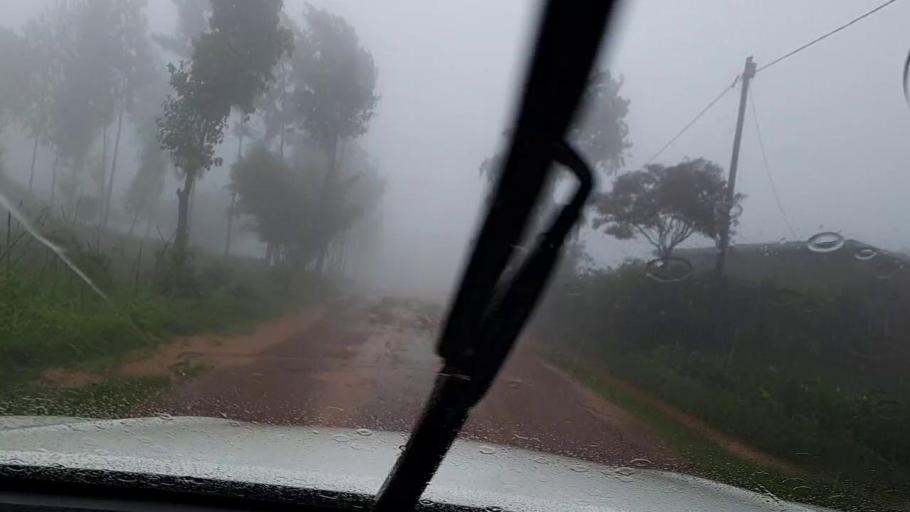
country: RW
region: Northern Province
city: Byumba
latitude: -1.7352
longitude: 30.0308
